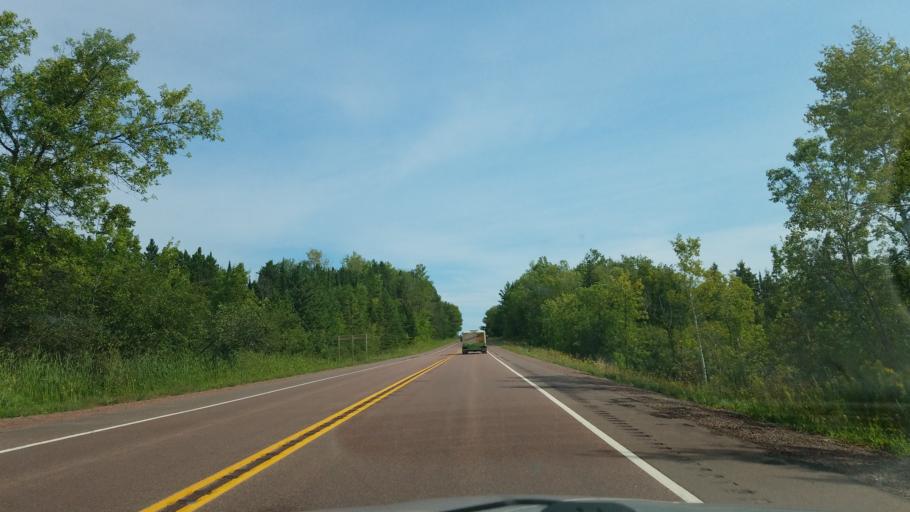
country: US
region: Wisconsin
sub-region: Ashland County
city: Ashland
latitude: 46.6027
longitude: -90.9532
